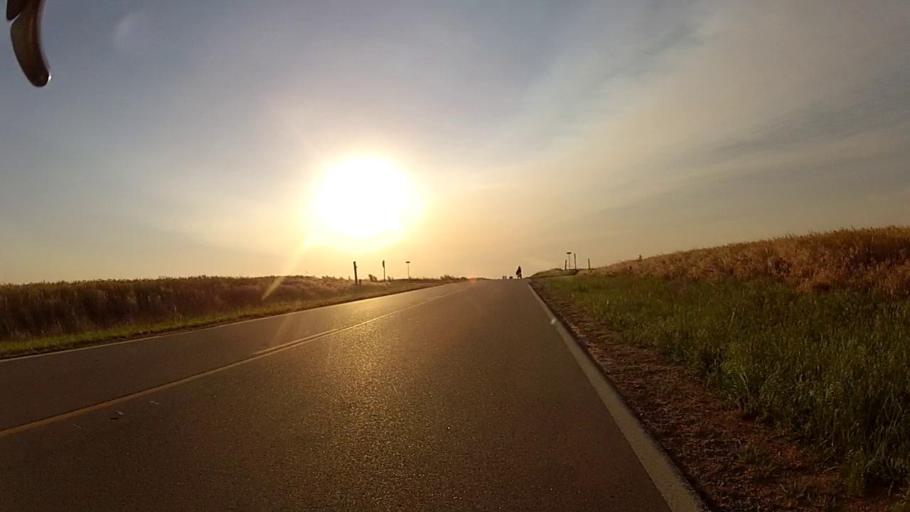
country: US
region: Kansas
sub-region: Harper County
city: Anthony
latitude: 37.1532
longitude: -97.9123
